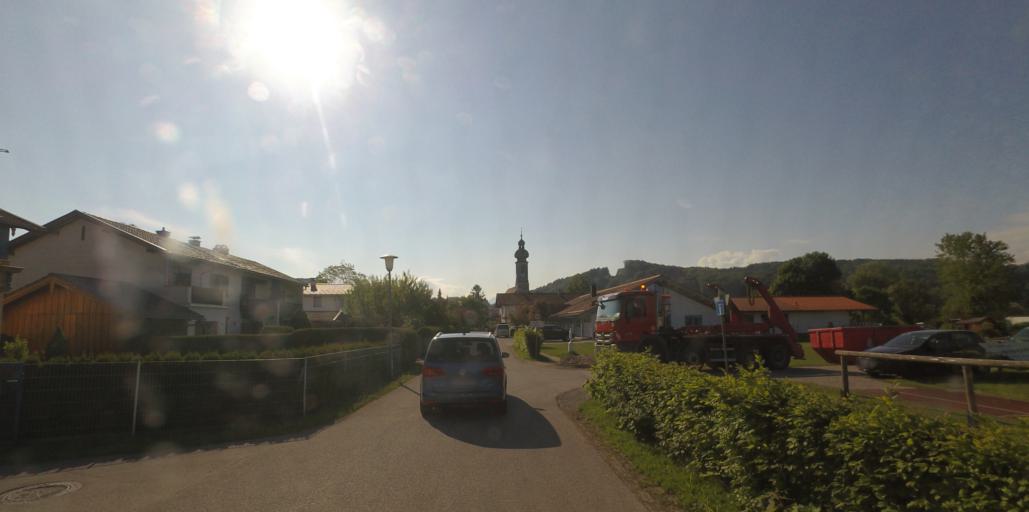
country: DE
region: Bavaria
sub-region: Upper Bavaria
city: Vachendorf
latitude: 47.8434
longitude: 12.6037
